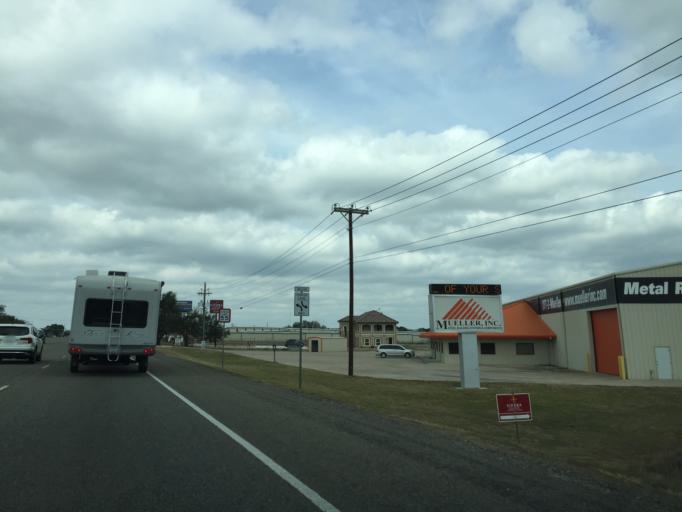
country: US
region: Texas
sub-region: Travis County
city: Briarcliff
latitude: 30.4588
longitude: -98.1558
